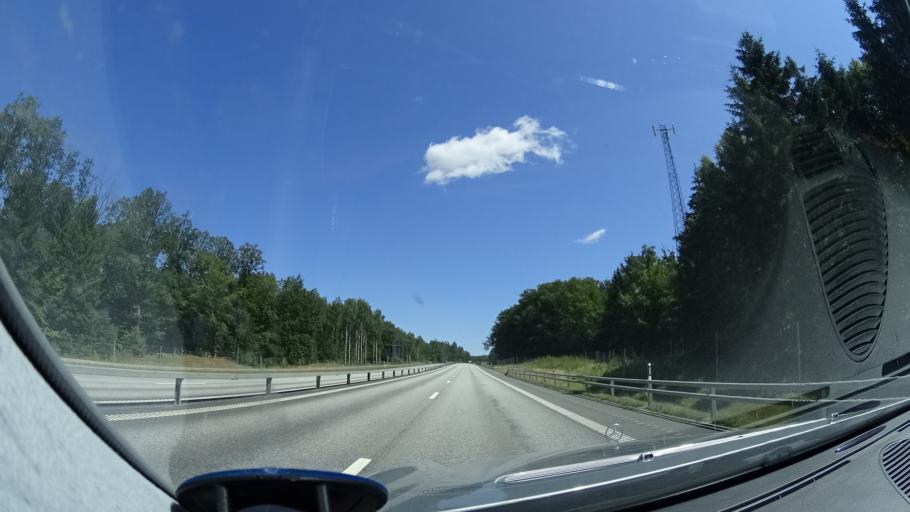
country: SE
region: Skane
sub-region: Horby Kommun
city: Hoerby
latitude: 55.9087
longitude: 13.7500
